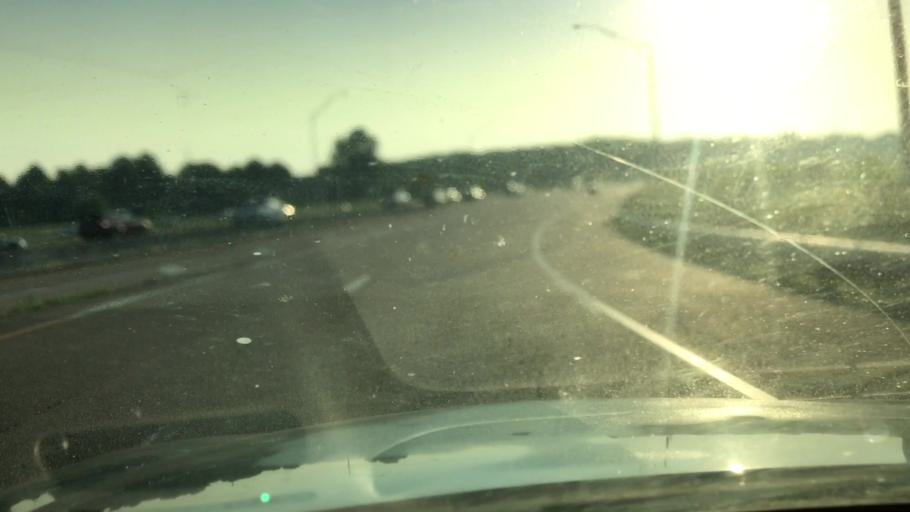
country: US
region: Tennessee
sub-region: Shelby County
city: New South Memphis
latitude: 35.0816
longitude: -89.9509
